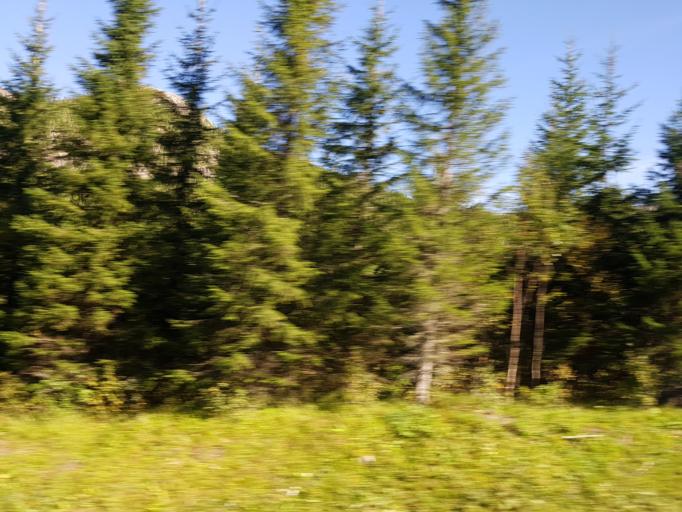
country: NO
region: Sor-Trondelag
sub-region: Afjord
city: A i Afjord
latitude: 63.7318
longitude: 10.2345
